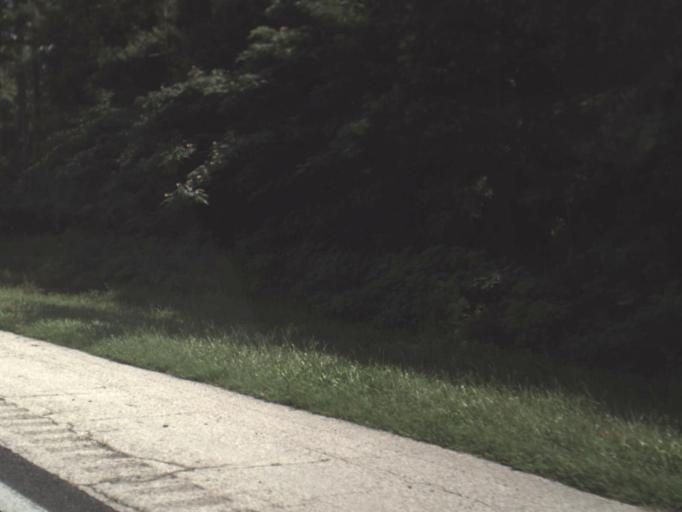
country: US
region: Florida
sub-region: Alachua County
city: High Springs
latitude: 29.8712
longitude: -82.5419
